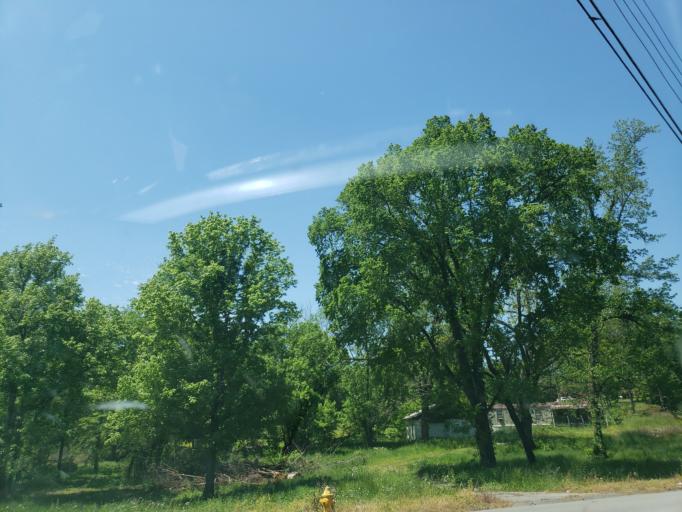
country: US
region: Alabama
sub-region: Madison County
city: Hazel Green
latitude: 34.9607
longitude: -86.5719
